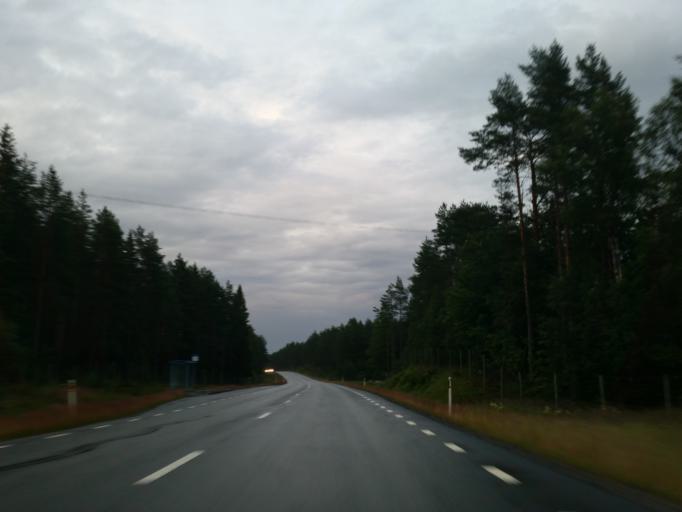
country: SE
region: Vaesterbotten
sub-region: Robertsfors Kommun
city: Robertsfors
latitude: 63.9958
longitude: 20.7770
